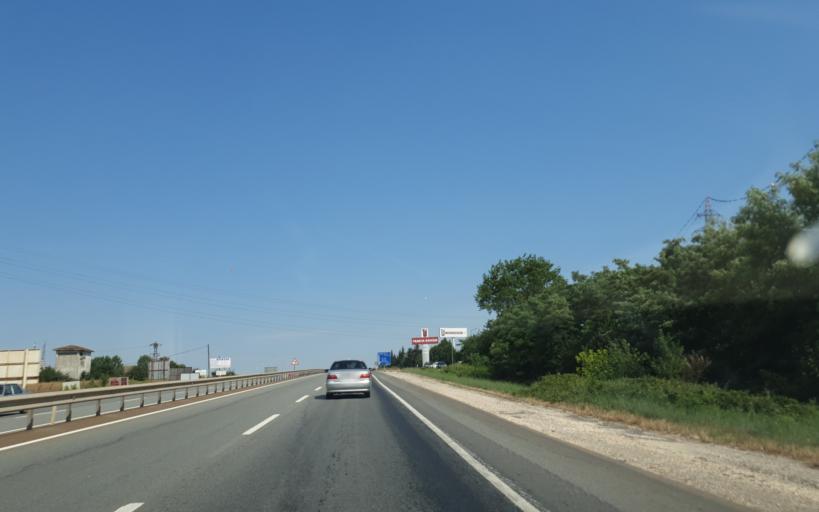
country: TR
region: Kirklareli
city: Buyukkaristiran
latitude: 41.2884
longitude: 27.5525
